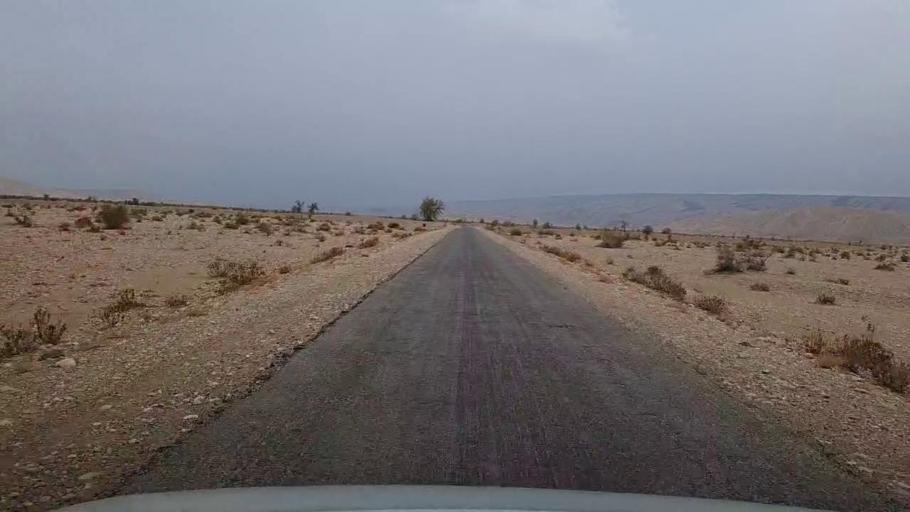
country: PK
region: Sindh
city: Sehwan
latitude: 26.2589
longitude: 67.7219
